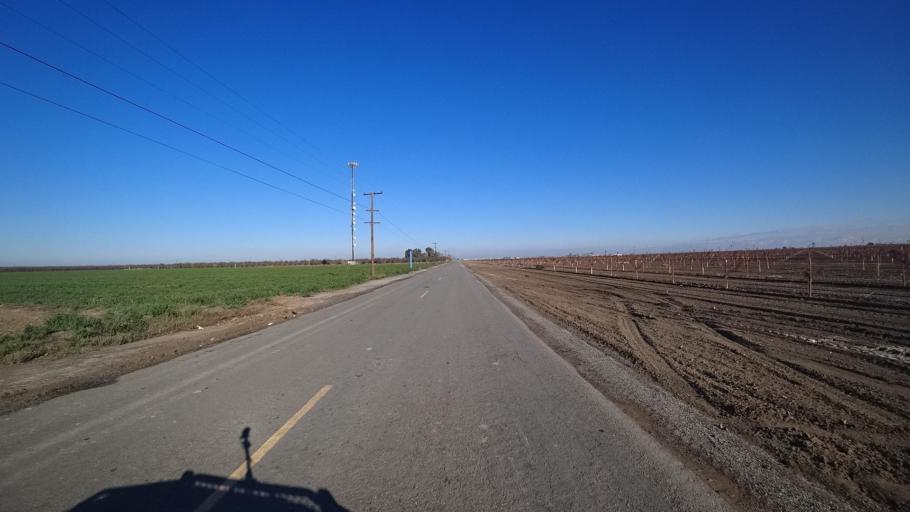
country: US
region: California
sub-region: Kern County
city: Delano
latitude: 35.7505
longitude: -119.3119
